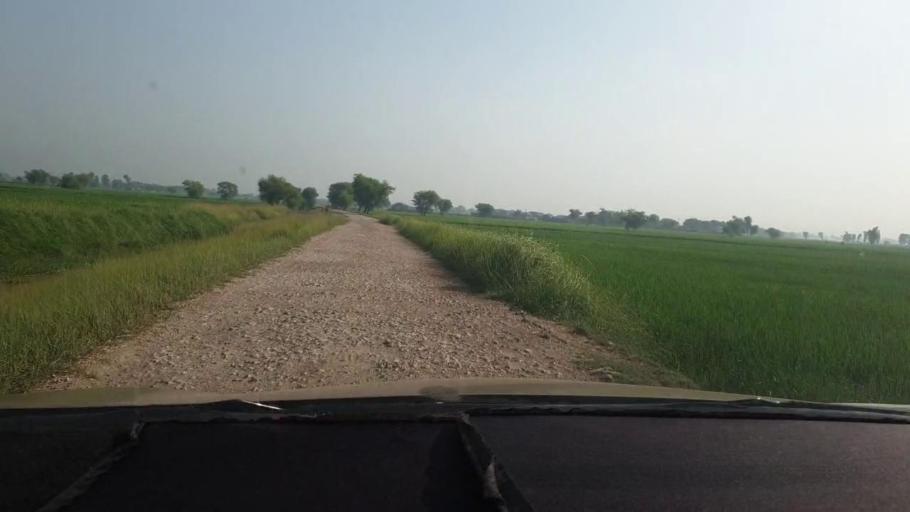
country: PK
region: Sindh
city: Kambar
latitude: 27.5906
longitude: 68.1054
